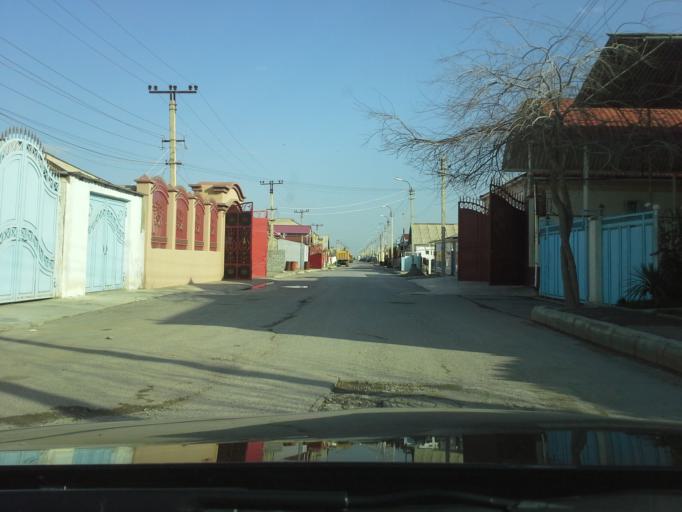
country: TM
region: Ahal
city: Abadan
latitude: 38.0194
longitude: 58.2284
